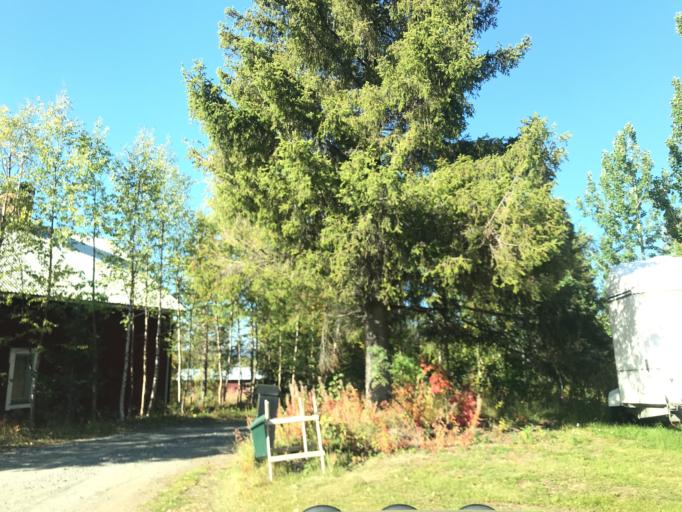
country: SE
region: Norrbotten
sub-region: Gallivare Kommun
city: Malmberget
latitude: 67.6450
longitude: 21.0673
